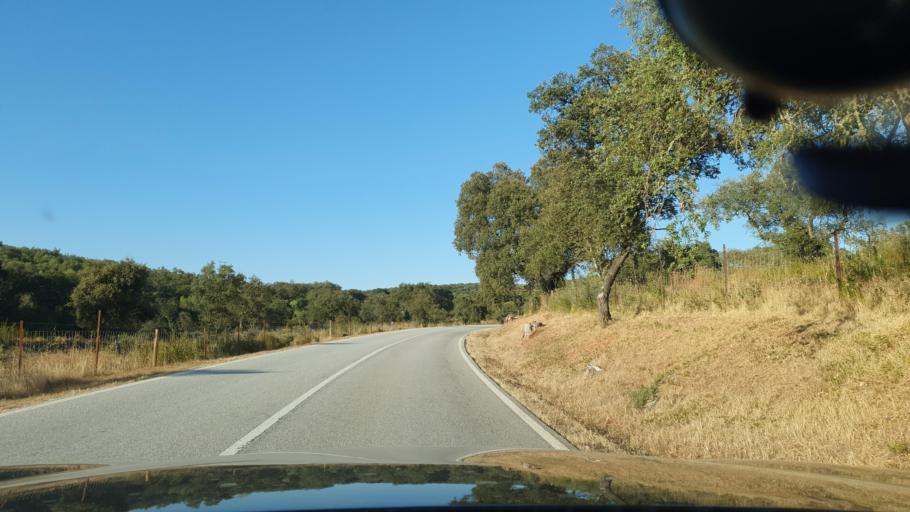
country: PT
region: Evora
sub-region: Estremoz
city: Estremoz
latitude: 38.9073
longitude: -7.6662
